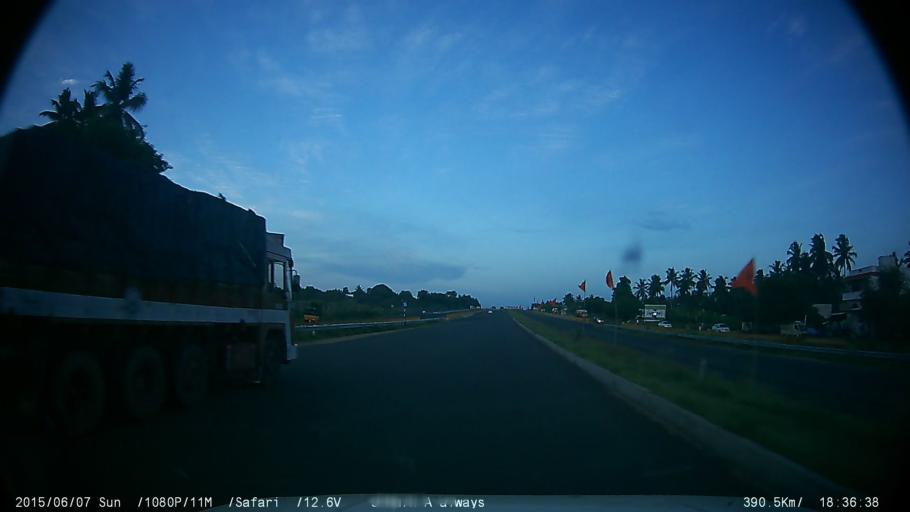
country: IN
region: Tamil Nadu
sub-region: Tiruppur
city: Avinashi
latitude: 11.1985
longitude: 77.3056
